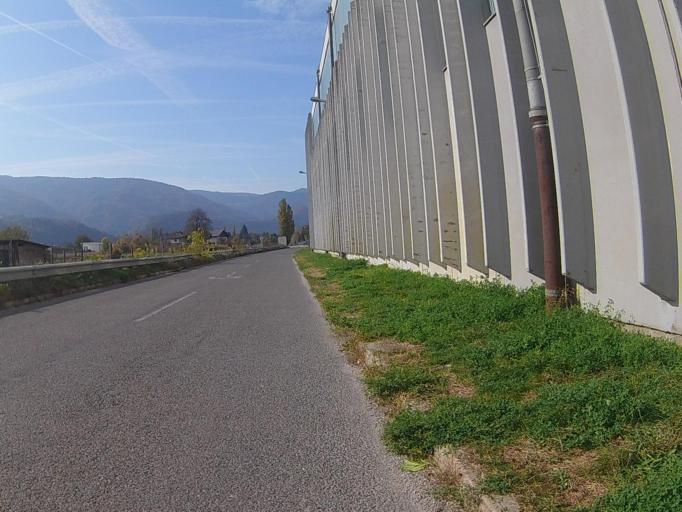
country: SI
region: Ruse
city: Ruse
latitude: 46.5464
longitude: 15.5181
